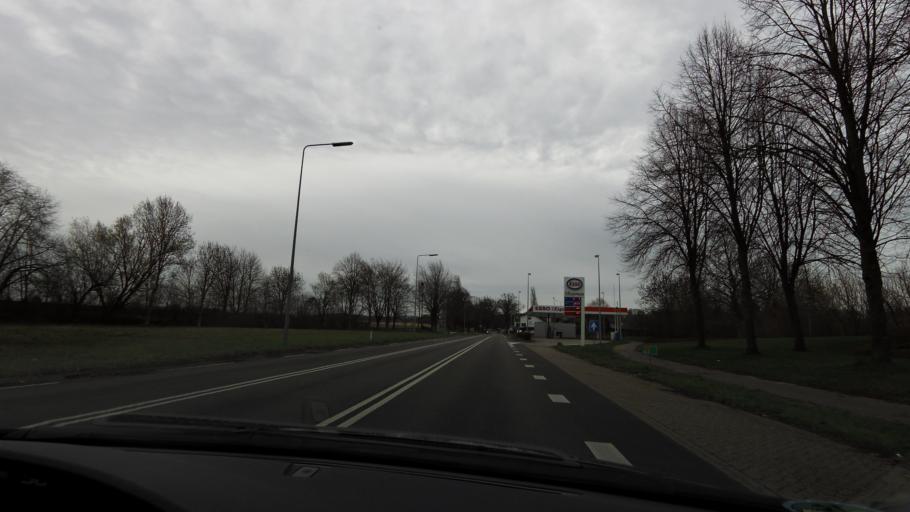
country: NL
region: Limburg
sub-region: Gemeente Maastricht
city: Heer
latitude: 50.8424
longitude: 5.7384
